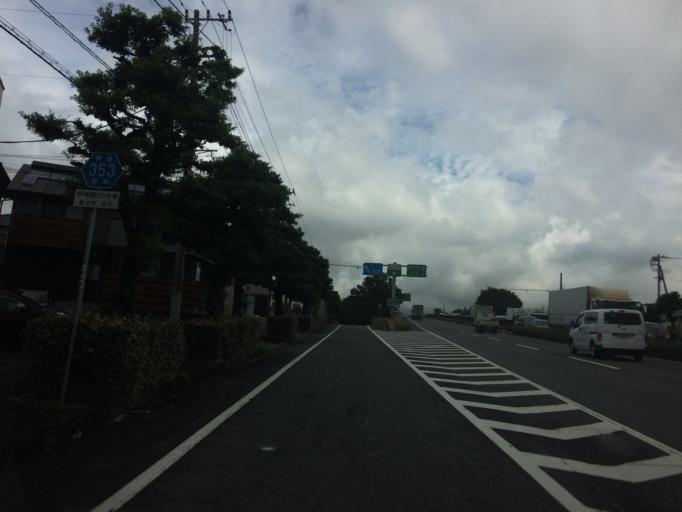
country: JP
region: Shizuoka
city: Fuji
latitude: 35.1708
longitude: 138.6723
